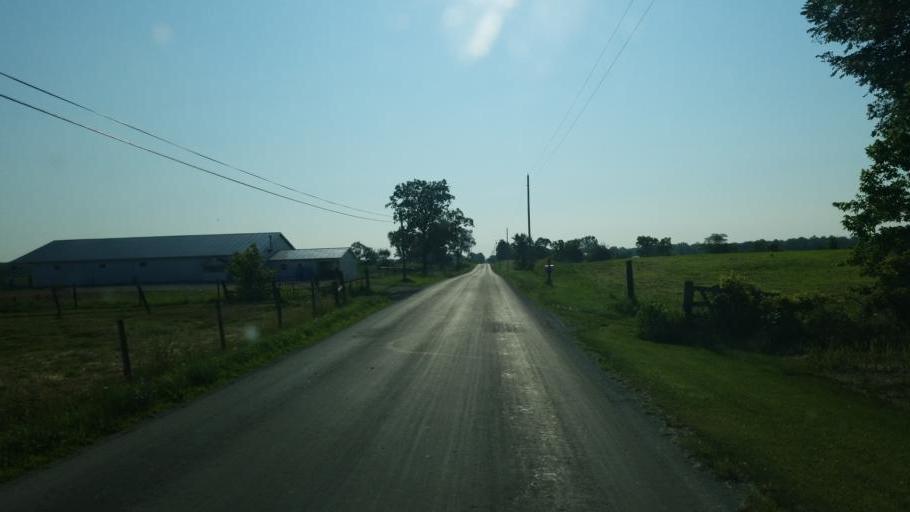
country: US
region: Ohio
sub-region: Hardin County
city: Kenton
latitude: 40.5635
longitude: -83.5342
